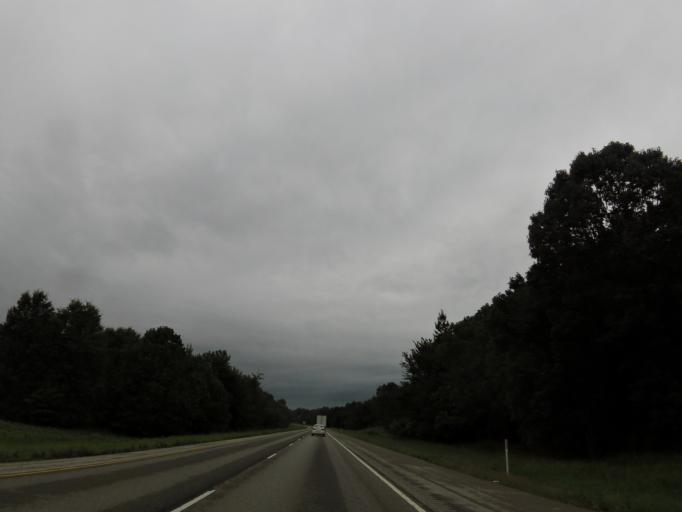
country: US
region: Illinois
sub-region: Massac County
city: Metropolis
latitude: 37.2527
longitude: -88.7216
